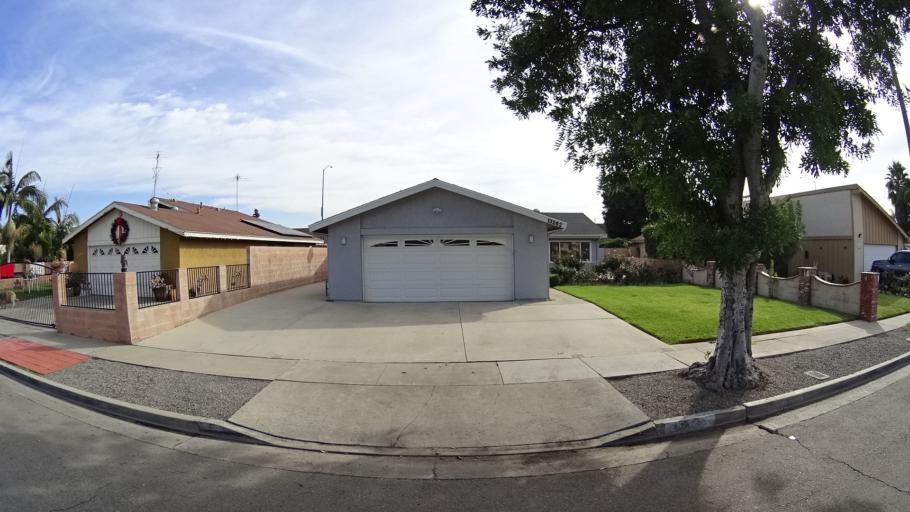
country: US
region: California
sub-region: Orange County
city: Garden Grove
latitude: 33.7771
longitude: -117.9014
